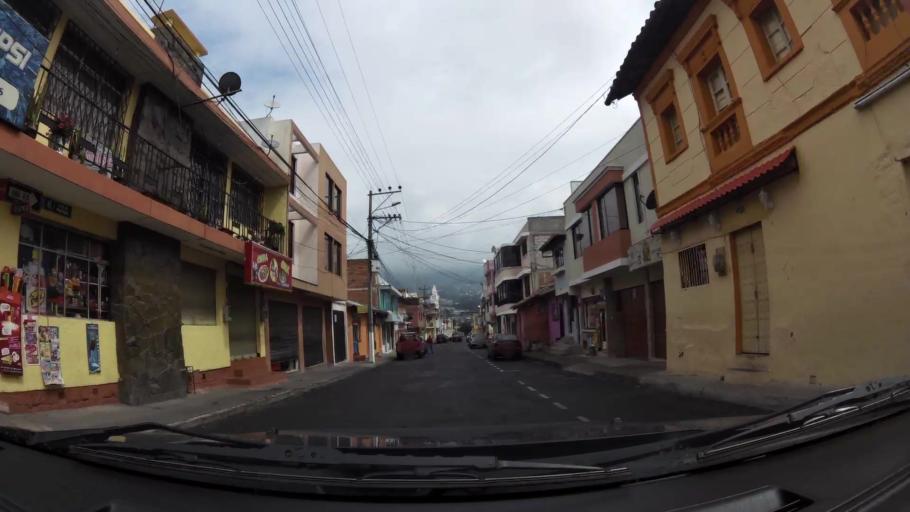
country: EC
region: Pichincha
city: Sangolqui
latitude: -0.2934
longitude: -78.4758
